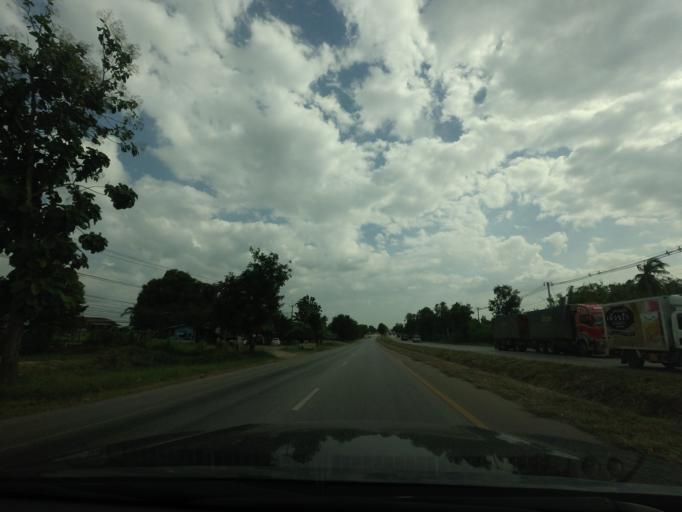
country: TH
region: Lop Buri
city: Chai Badan
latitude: 15.2403
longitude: 101.1262
